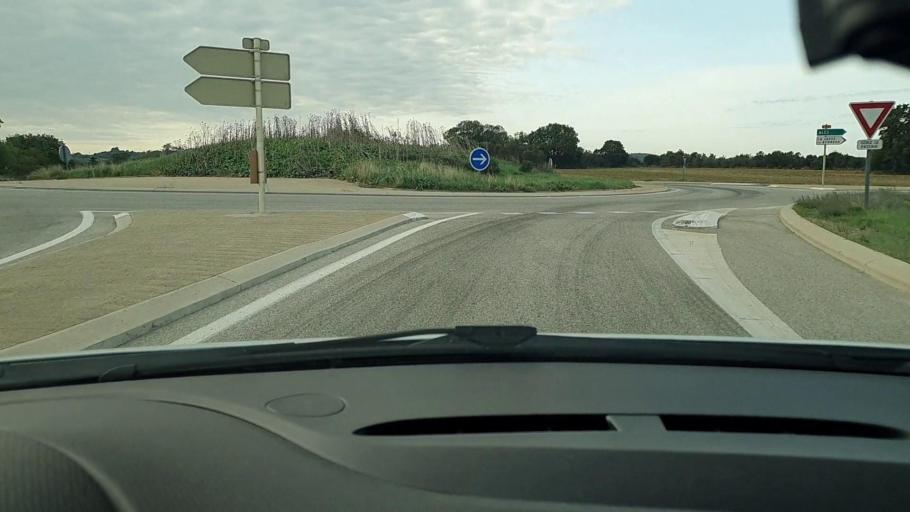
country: FR
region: Languedoc-Roussillon
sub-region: Departement du Gard
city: Mons
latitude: 44.0762
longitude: 4.2195
